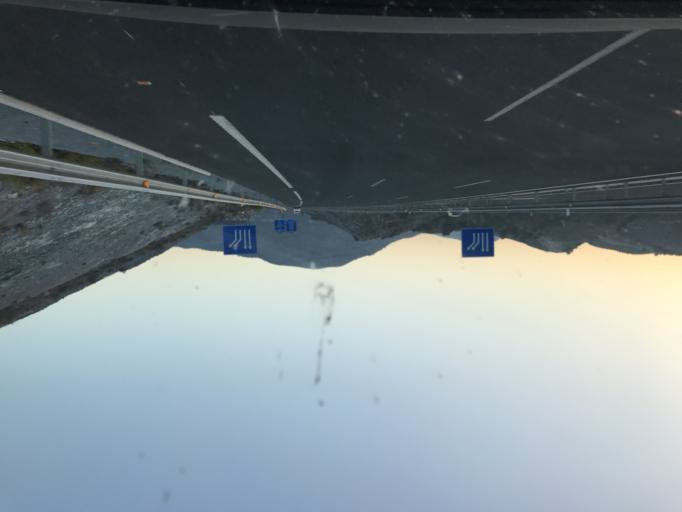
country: ES
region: Andalusia
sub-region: Provincia de Granada
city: Motril
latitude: 36.7783
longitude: -3.5007
